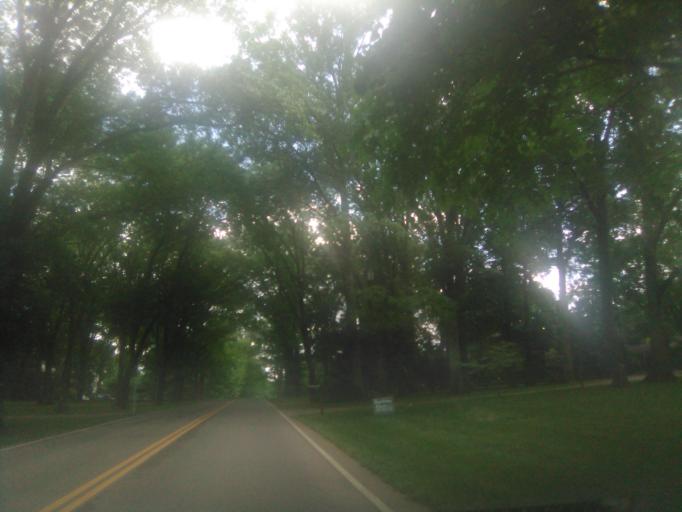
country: US
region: Tennessee
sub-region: Davidson County
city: Belle Meade
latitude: 36.0993
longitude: -86.8462
